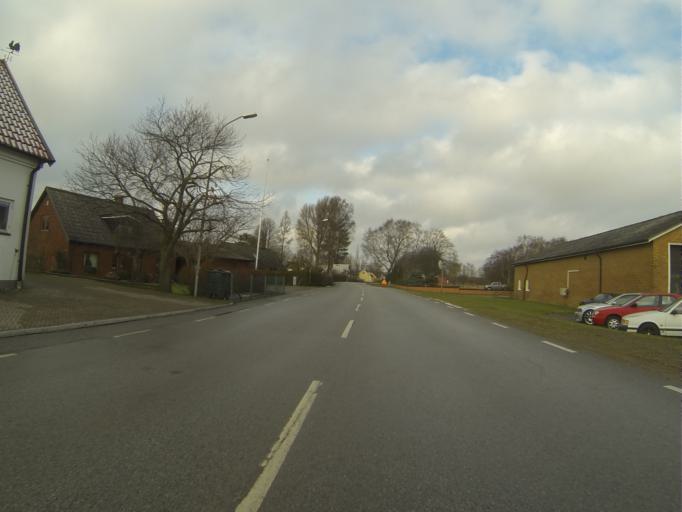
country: SE
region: Skane
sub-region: Svedala Kommun
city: Klagerup
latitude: 55.5531
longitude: 13.2752
